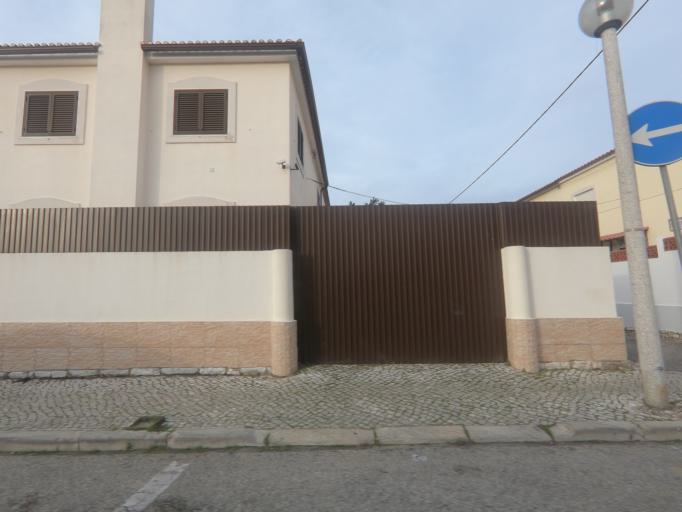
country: PT
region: Setubal
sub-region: Setubal
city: Setubal
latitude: 38.5246
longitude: -8.8781
